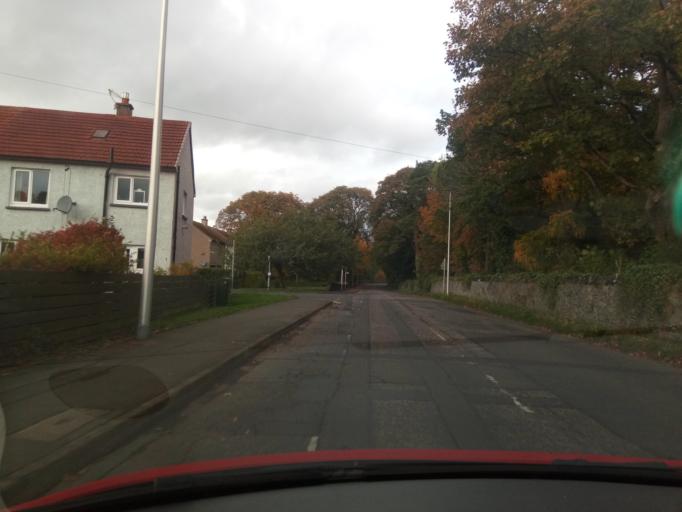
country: GB
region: Scotland
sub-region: The Scottish Borders
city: Peebles
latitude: 55.6473
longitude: -3.1813
